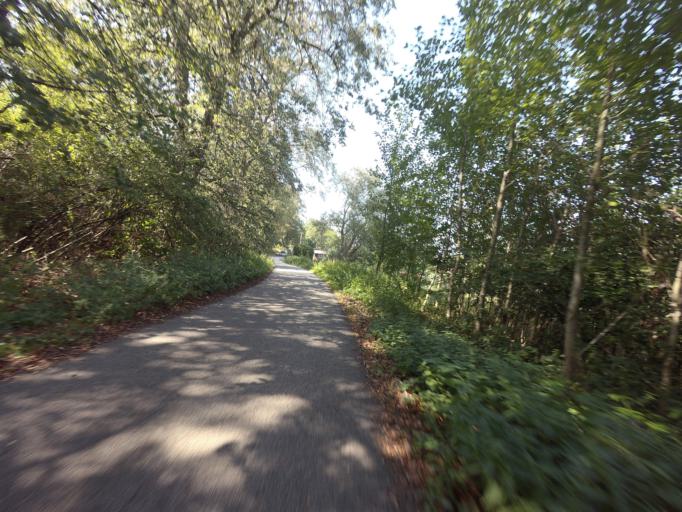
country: CZ
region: Jihocesky
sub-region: Okres Ceske Budejovice
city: Hluboka nad Vltavou
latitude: 49.1229
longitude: 14.4562
